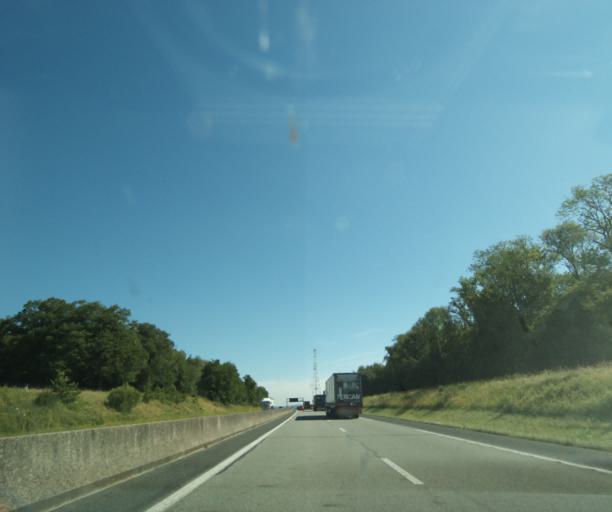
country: FR
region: Lorraine
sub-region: Departement des Vosges
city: Lamarche
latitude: 48.1122
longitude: 5.6583
